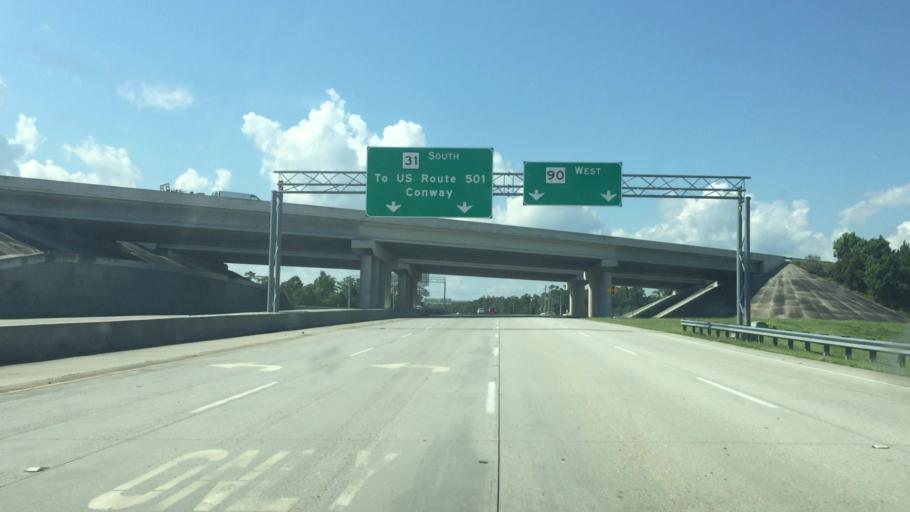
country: US
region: South Carolina
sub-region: Horry County
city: North Myrtle Beach
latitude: 33.8433
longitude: -78.7008
